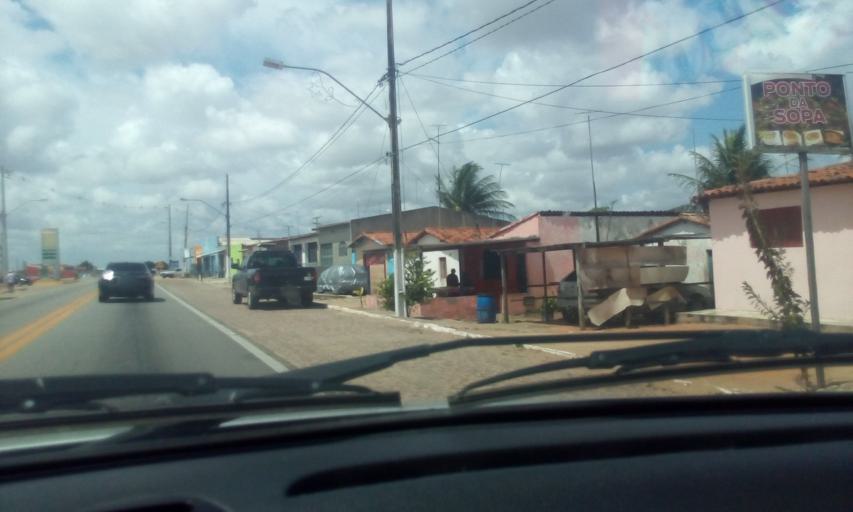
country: BR
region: Rio Grande do Norte
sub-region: Sao Paulo Do Potengi
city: Sao Paulo do Potengi
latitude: -5.9865
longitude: -35.5865
